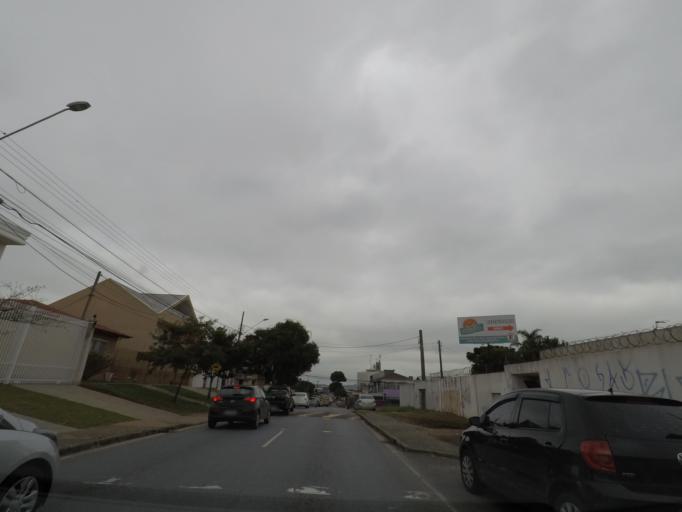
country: BR
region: Parana
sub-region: Curitiba
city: Curitiba
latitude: -25.4781
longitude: -49.3089
